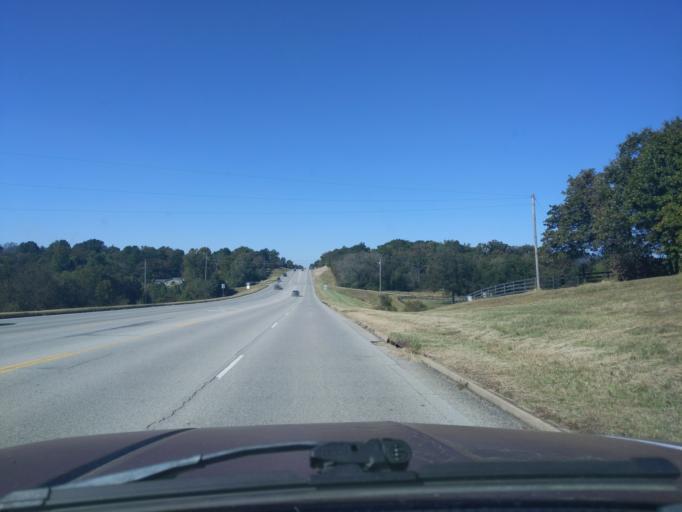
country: US
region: Oklahoma
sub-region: Creek County
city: Kiefer
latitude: 35.9885
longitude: -96.0626
